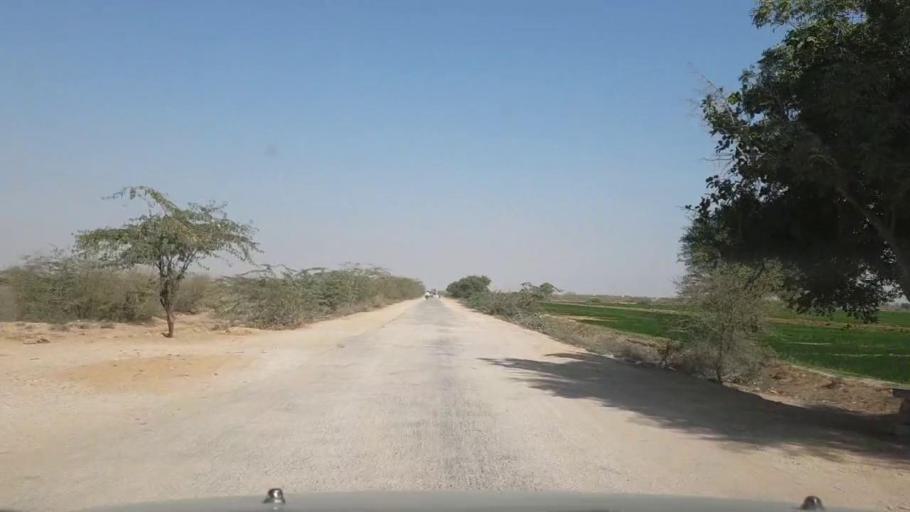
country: PK
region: Sindh
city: Thatta
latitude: 24.9572
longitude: 67.9575
